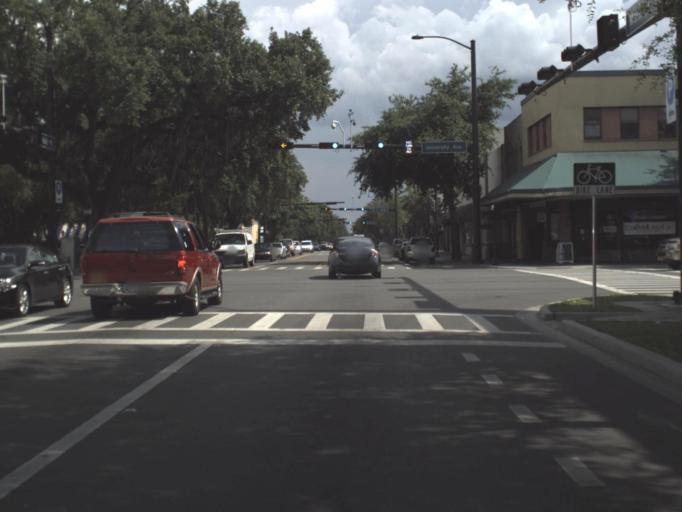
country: US
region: Florida
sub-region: Alachua County
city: Gainesville
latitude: 29.6523
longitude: -82.3251
